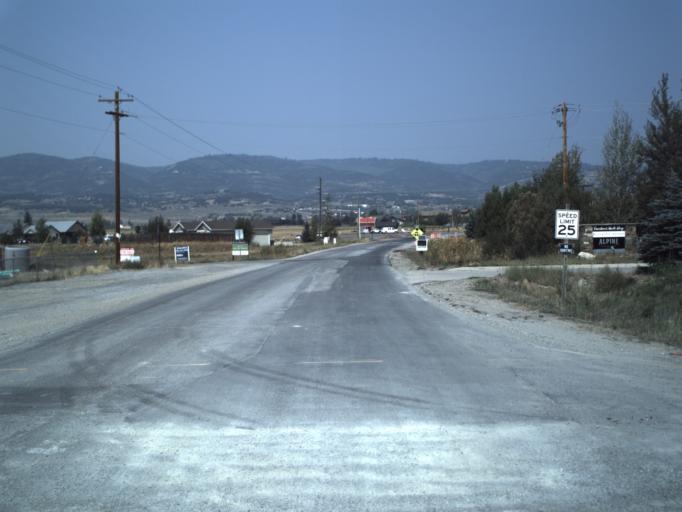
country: US
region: Utah
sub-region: Summit County
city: Snyderville
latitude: 40.7343
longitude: -111.4995
